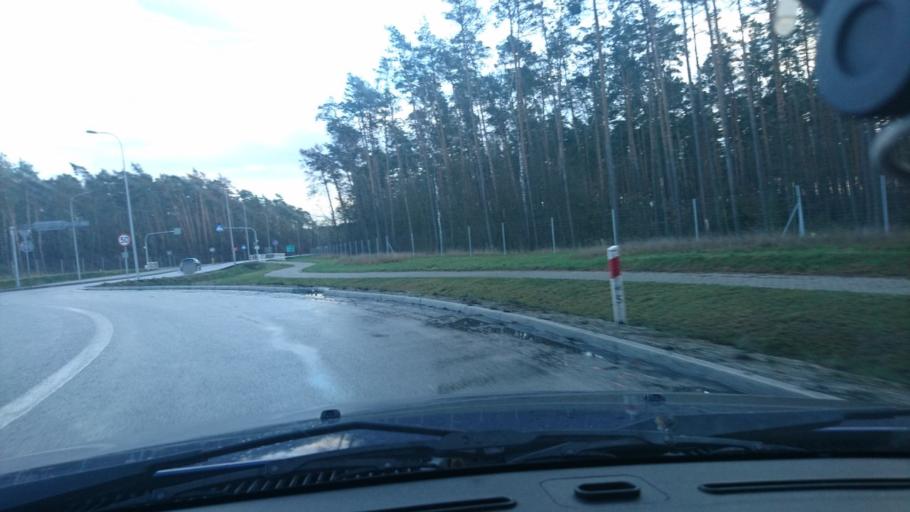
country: PL
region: Greater Poland Voivodeship
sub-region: Powiat kepinski
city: Kepno
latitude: 51.3311
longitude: 17.9582
